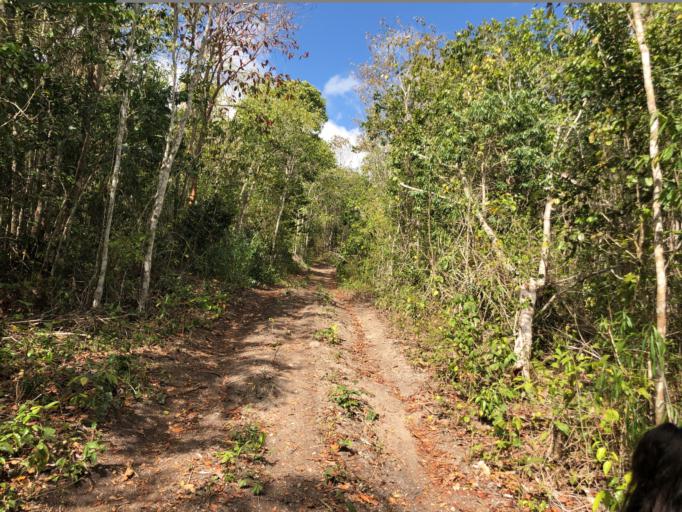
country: MX
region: Quintana Roo
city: Nicolas Bravo
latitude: 18.4471
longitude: -89.3093
